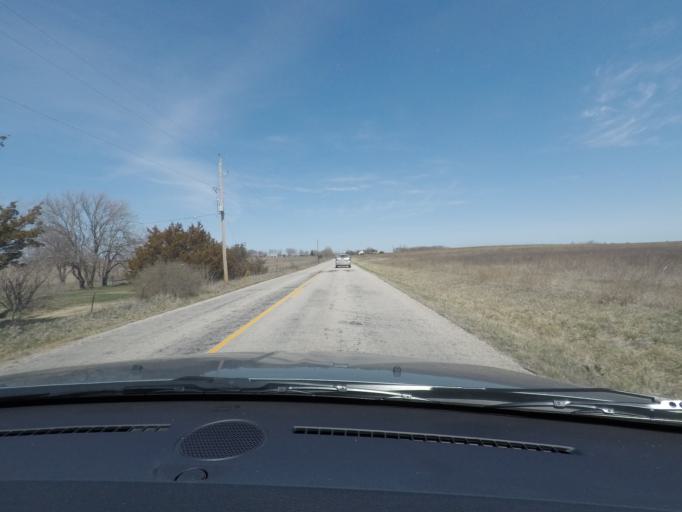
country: US
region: Kansas
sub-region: Lyon County
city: Emporia
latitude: 38.6225
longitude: -96.1696
